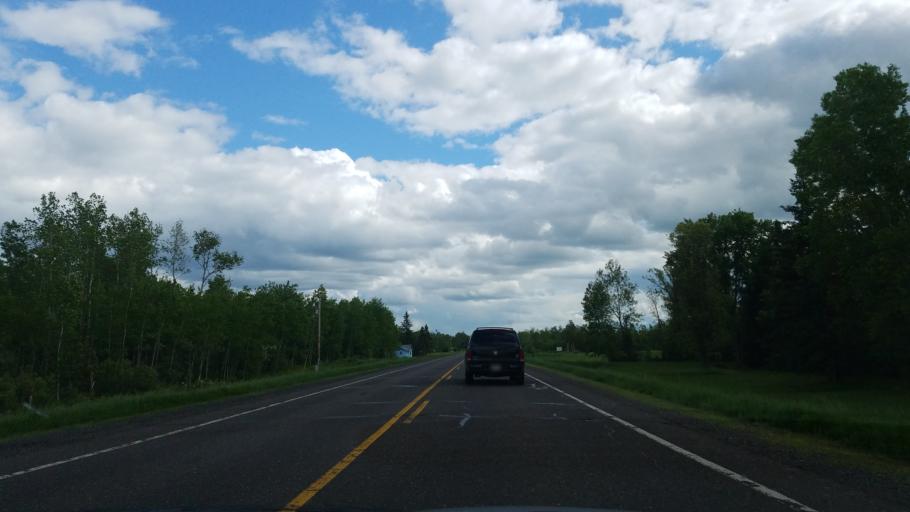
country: US
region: Wisconsin
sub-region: Burnett County
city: Siren
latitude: 46.1624
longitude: -92.2381
